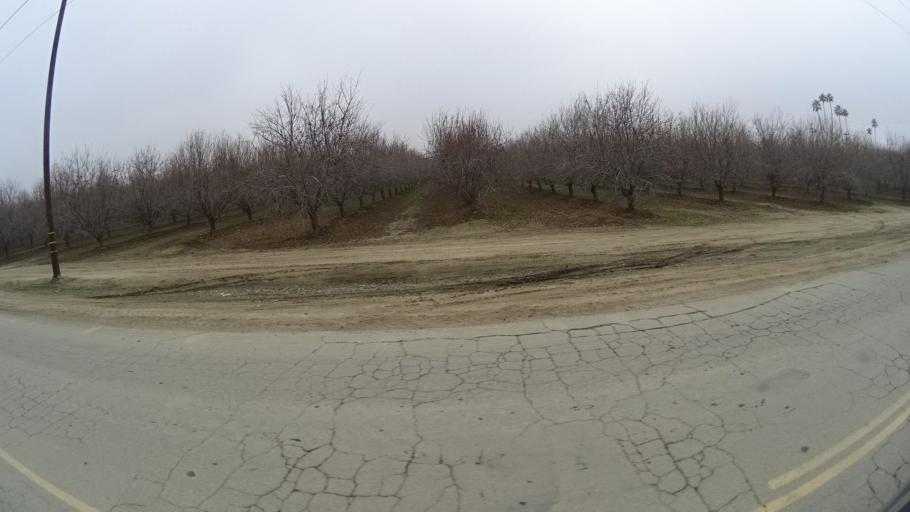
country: US
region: California
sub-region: Kern County
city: Greenfield
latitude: 35.2379
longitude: -119.0556
